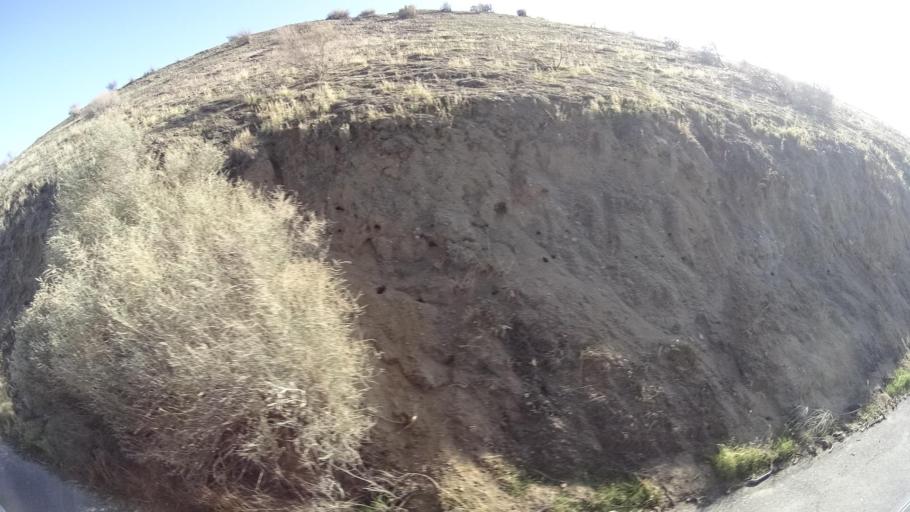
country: US
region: California
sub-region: Kern County
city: Taft Heights
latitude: 35.1276
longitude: -119.4718
